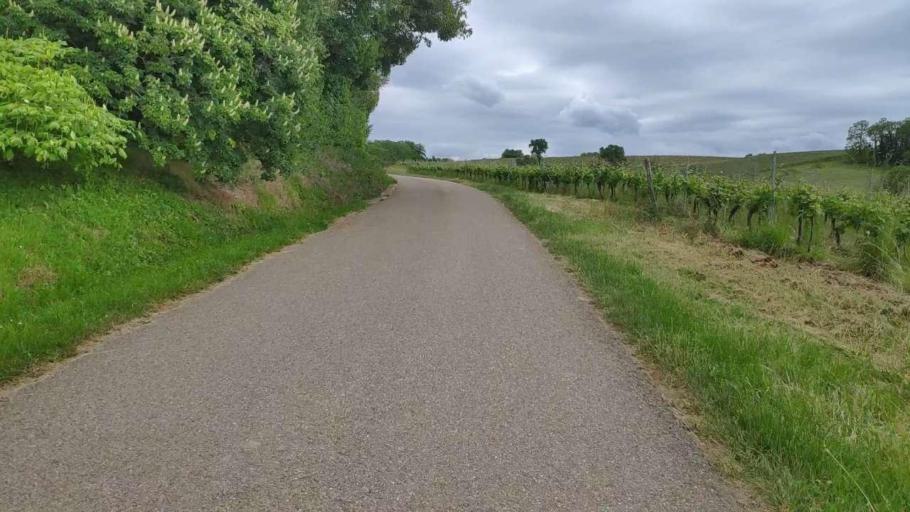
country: FR
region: Franche-Comte
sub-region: Departement du Jura
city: Bletterans
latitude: 46.7498
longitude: 5.5237
